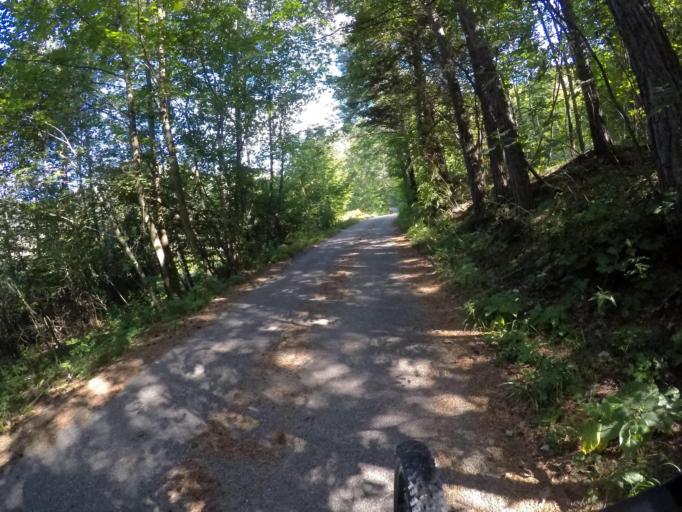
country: IT
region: Friuli Venezia Giulia
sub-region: Provincia di Udine
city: Zuglio
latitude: 46.4425
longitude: 13.0898
